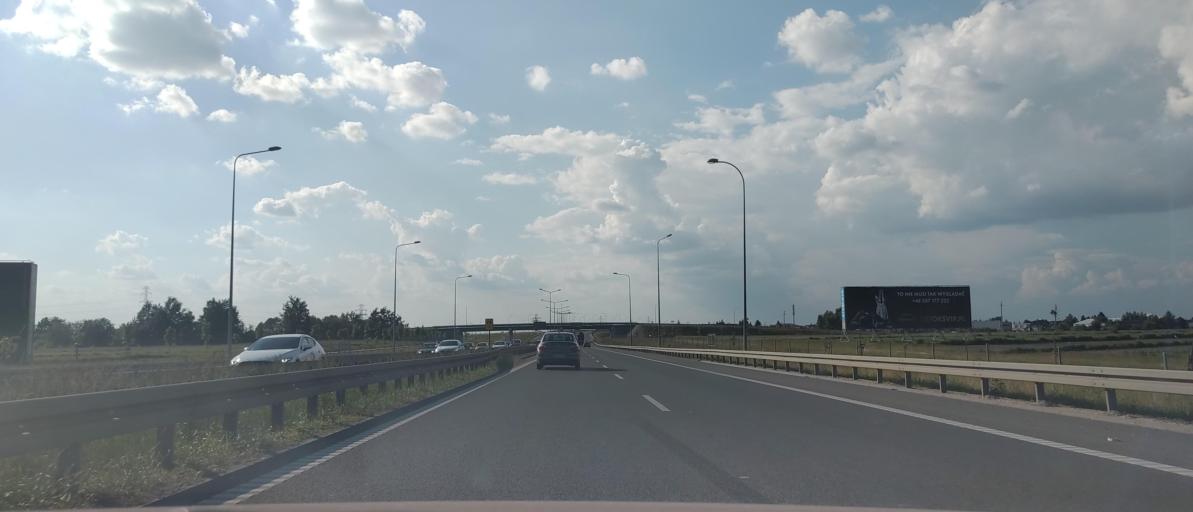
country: PL
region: Masovian Voivodeship
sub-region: Powiat pruszkowski
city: Nowe Grocholice
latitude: 52.1192
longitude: 20.8858
